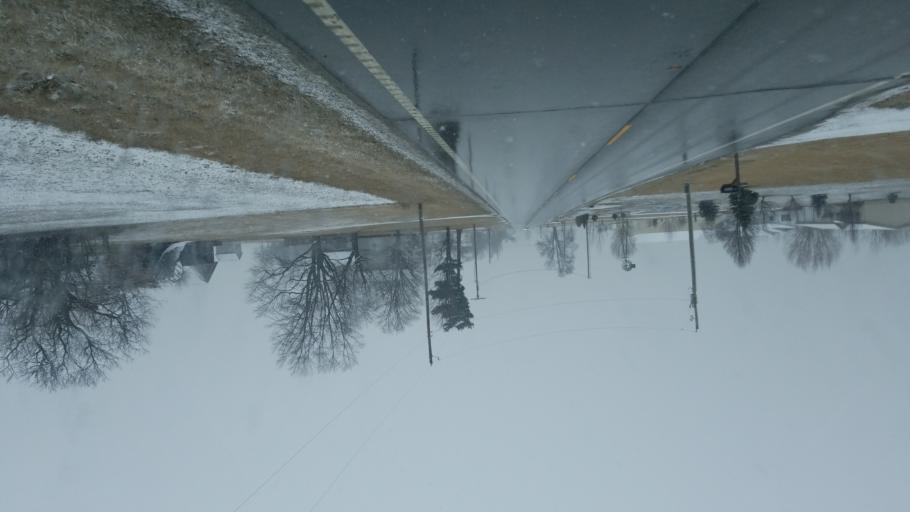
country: US
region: Ohio
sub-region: Defiance County
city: Hicksville
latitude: 41.3117
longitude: -84.7475
